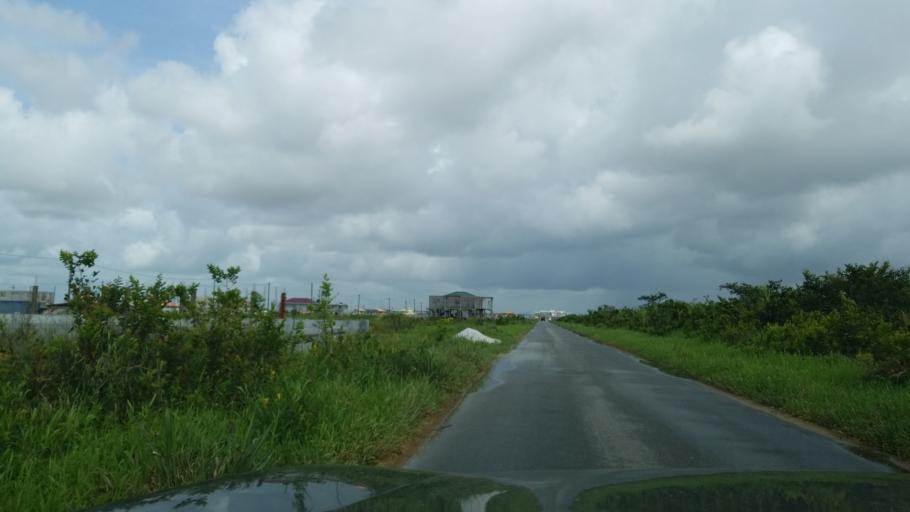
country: GY
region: Demerara-Mahaica
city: Georgetown
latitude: 6.7560
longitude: -58.1568
